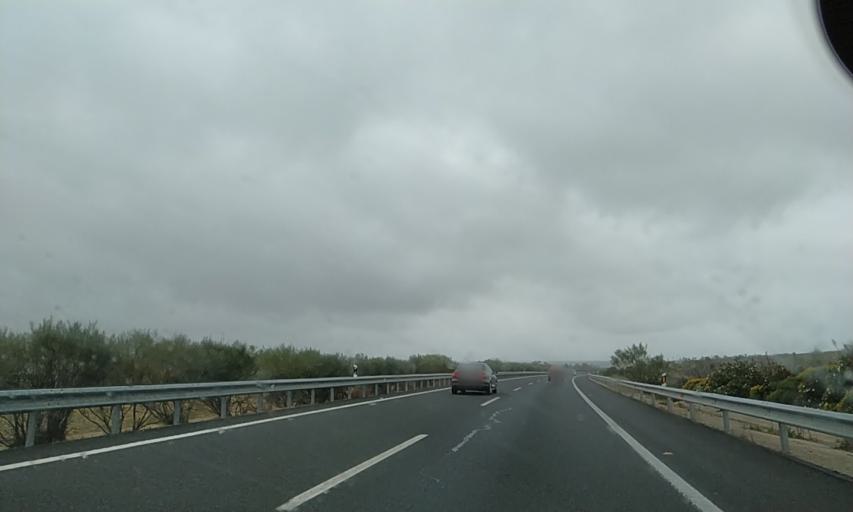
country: ES
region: Extremadura
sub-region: Provincia de Caceres
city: Canaveral
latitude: 39.7511
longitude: -6.4008
